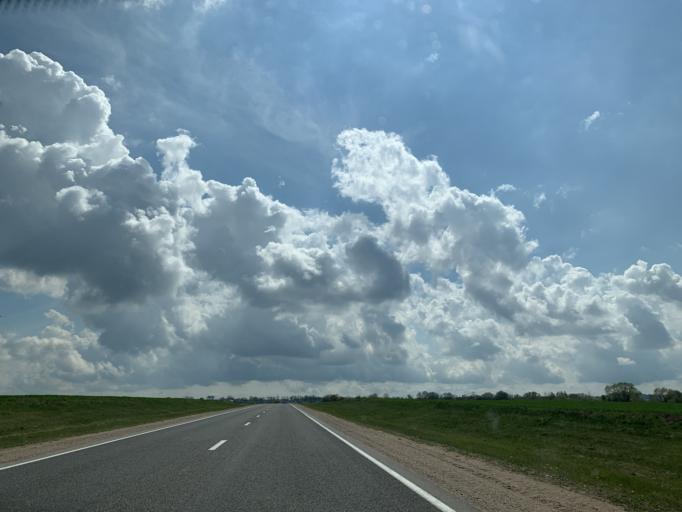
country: BY
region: Minsk
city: Nyasvizh
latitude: 53.2383
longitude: 26.7134
